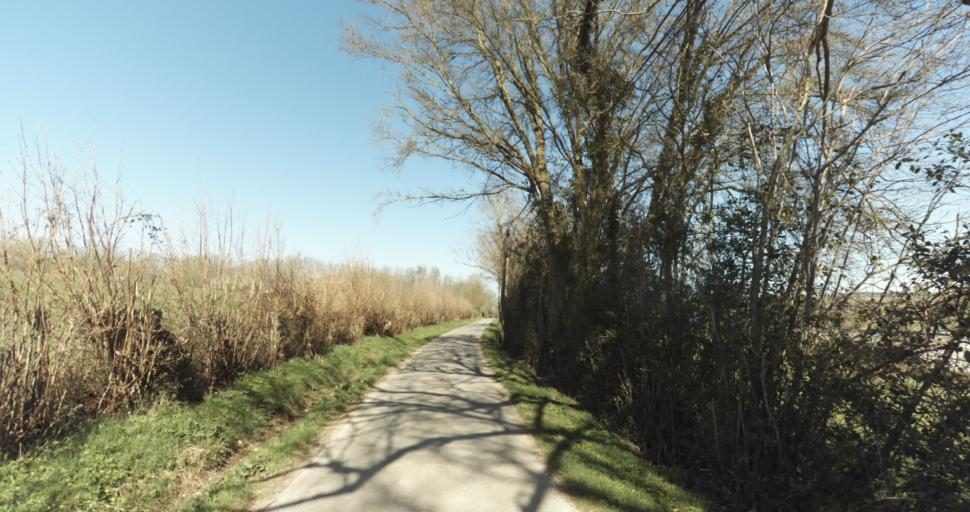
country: FR
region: Lower Normandy
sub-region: Departement du Calvados
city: Livarot
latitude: 49.0031
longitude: 0.0896
